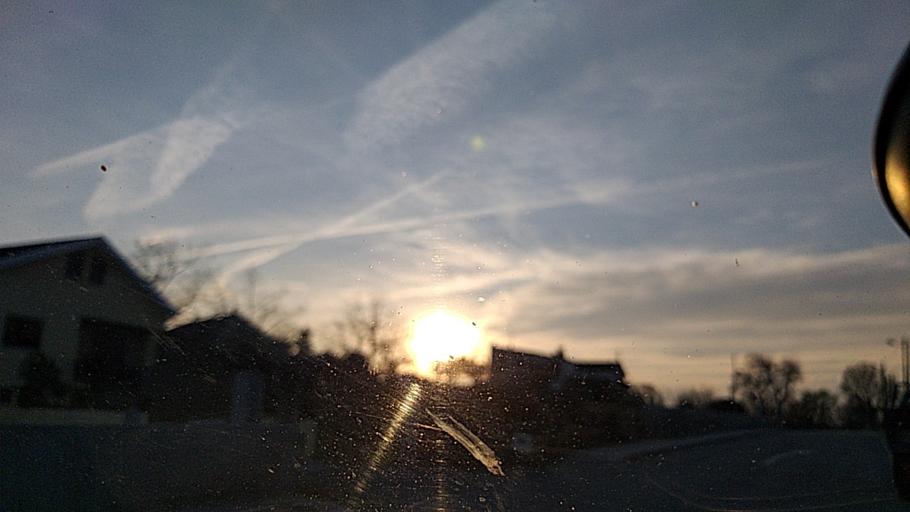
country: PT
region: Guarda
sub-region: Guarda
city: Sequeira
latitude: 40.6036
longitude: -7.0759
